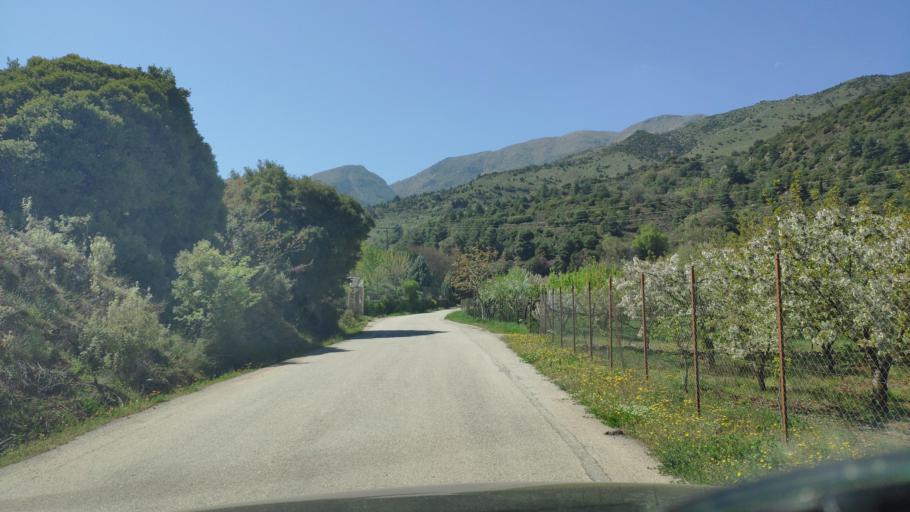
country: GR
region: West Greece
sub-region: Nomos Achaias
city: Akrata
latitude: 38.0921
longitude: 22.3240
